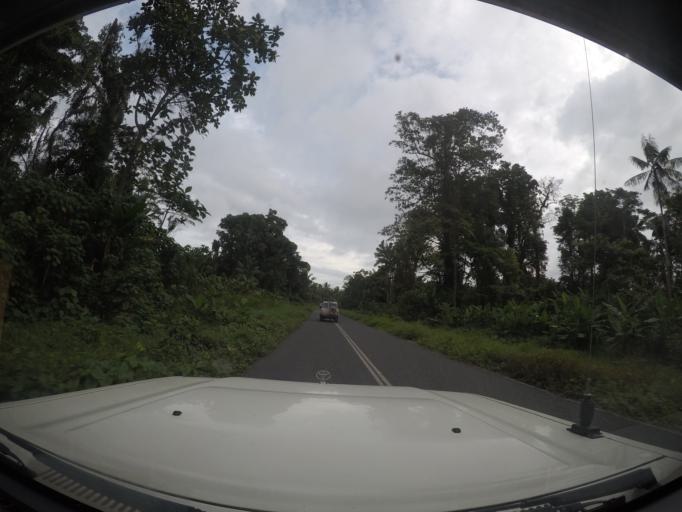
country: PG
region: Gulf
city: Kerema
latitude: -8.0313
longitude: 145.9365
